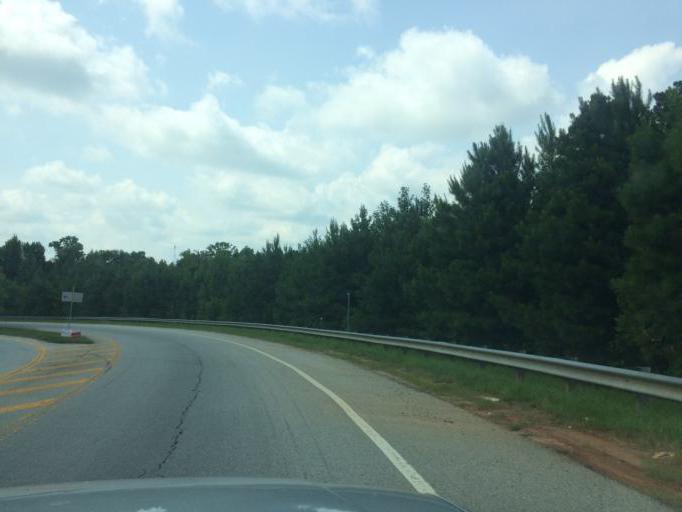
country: US
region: South Carolina
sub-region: Greenville County
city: Fountain Inn
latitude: 34.6430
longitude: -82.1465
